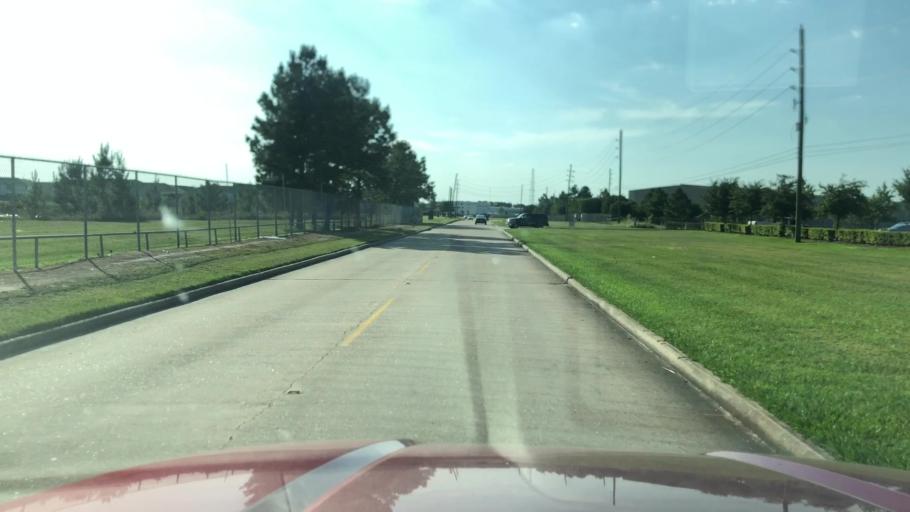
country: US
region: Texas
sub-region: Harris County
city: Hudson
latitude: 29.9436
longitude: -95.4916
